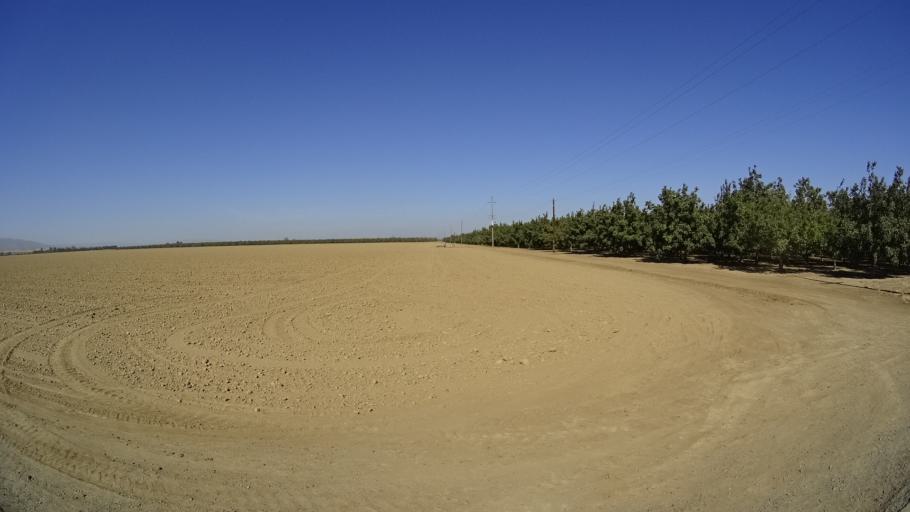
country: US
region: California
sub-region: Yolo County
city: Winters
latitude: 38.5838
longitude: -121.9624
